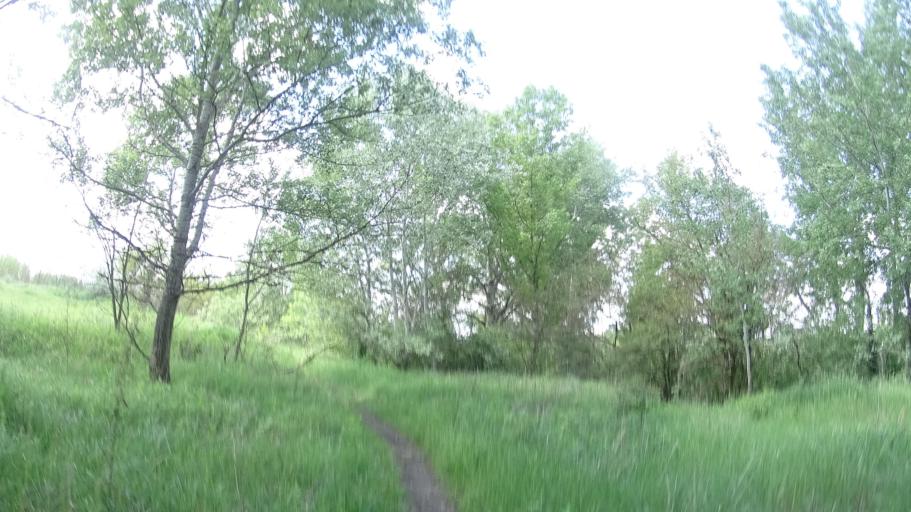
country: HU
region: Komarom-Esztergom
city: Dorog
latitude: 47.7261
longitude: 18.7548
